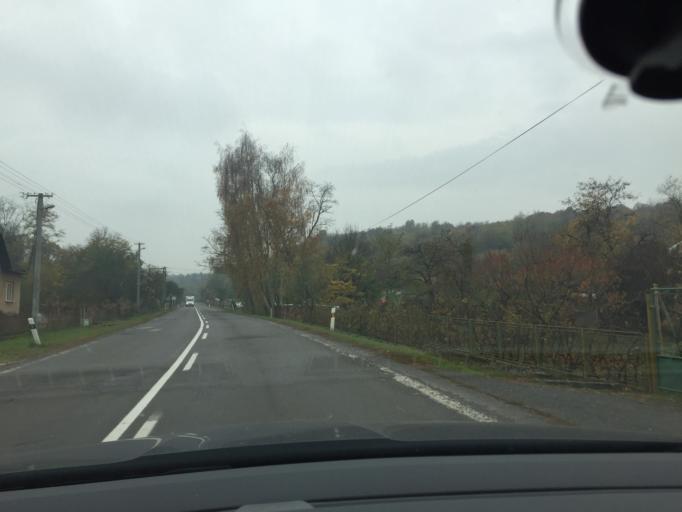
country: SK
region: Banskobystricky
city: Velky Krtis
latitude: 48.2888
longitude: 19.4861
